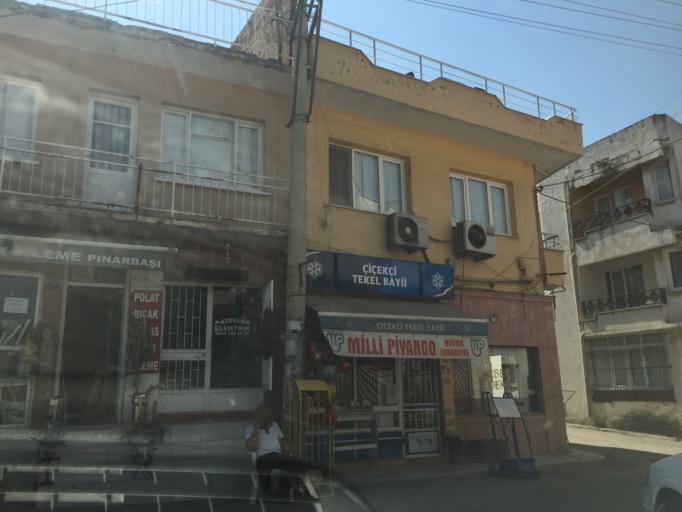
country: TR
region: Izmir
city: Bornova
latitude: 38.4287
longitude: 27.2666
